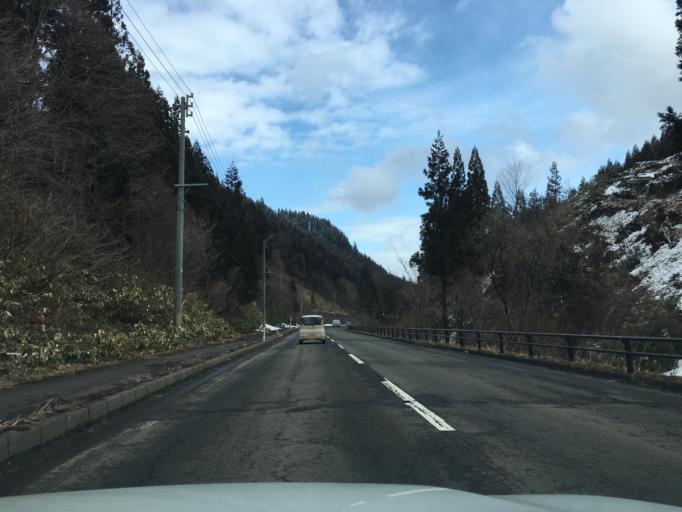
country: JP
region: Akita
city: Takanosu
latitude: 39.9928
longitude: 140.2489
